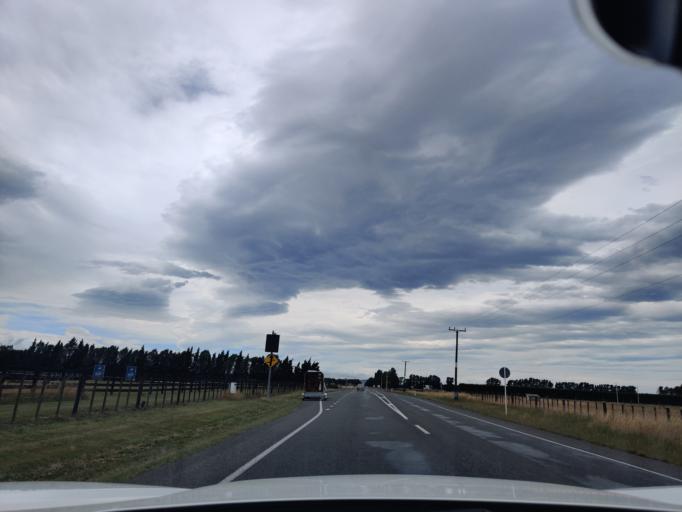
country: NZ
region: Wellington
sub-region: Masterton District
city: Masterton
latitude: -40.9824
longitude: 175.5831
